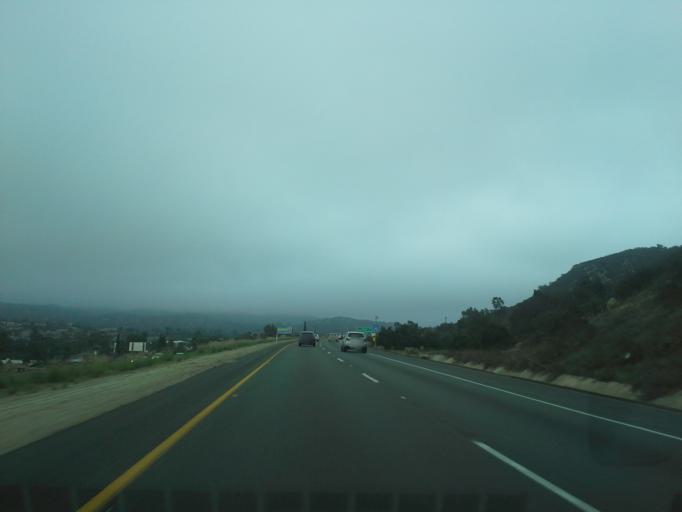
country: US
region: California
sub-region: San Diego County
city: Harbison Canyon
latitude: 32.8550
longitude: -116.8353
